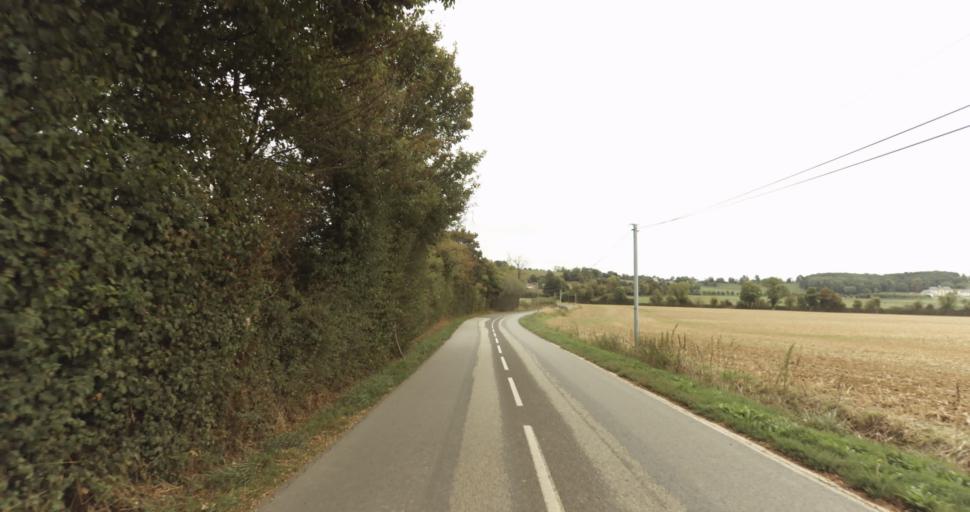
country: FR
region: Lower Normandy
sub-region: Departement de l'Orne
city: Gace
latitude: 48.7087
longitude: 0.3150
